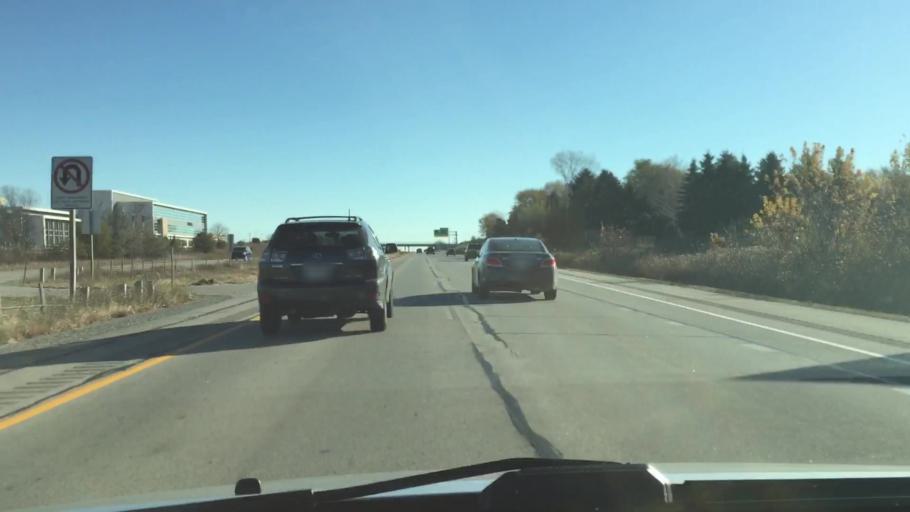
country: US
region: Wisconsin
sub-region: Outagamie County
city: Appleton
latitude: 44.2987
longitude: -88.4262
